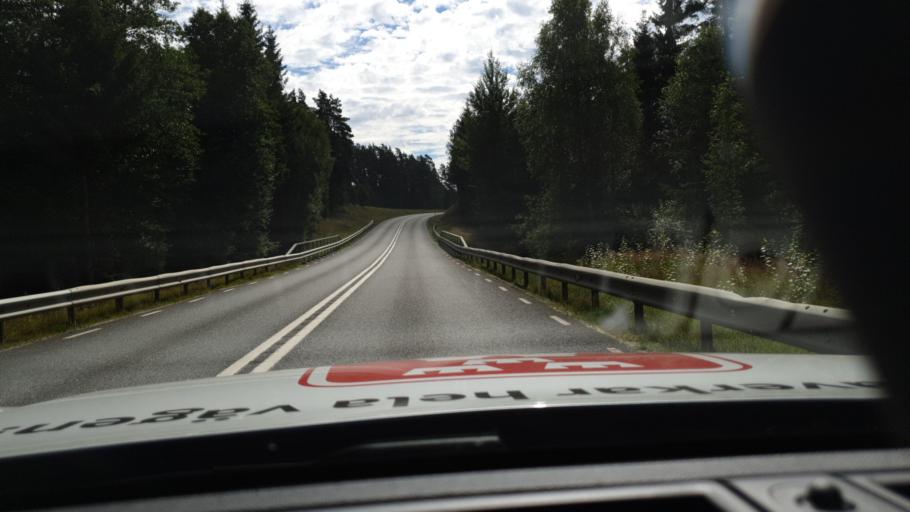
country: SE
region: Joenkoeping
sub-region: Vaggeryds Kommun
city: Vaggeryd
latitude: 57.4804
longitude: 14.3094
